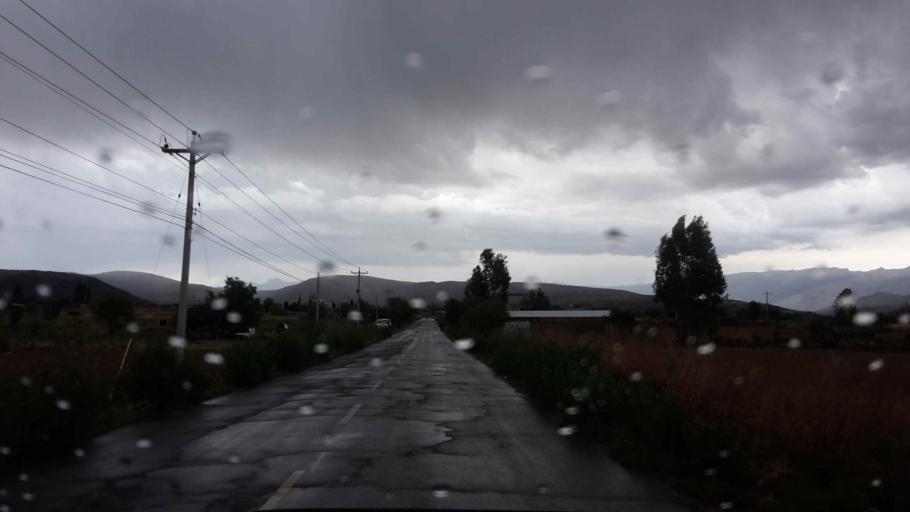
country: BO
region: Cochabamba
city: Tarata
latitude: -17.5641
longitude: -66.0791
